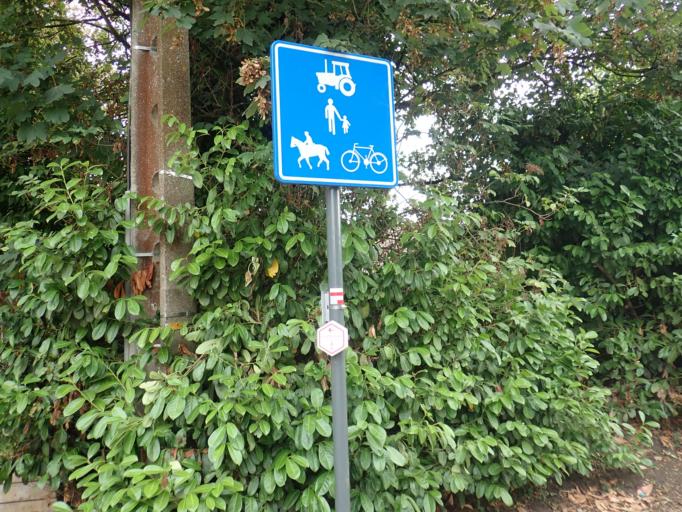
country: BE
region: Flanders
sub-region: Provincie Vlaams-Brabant
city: Asse
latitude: 50.9296
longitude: 4.2154
